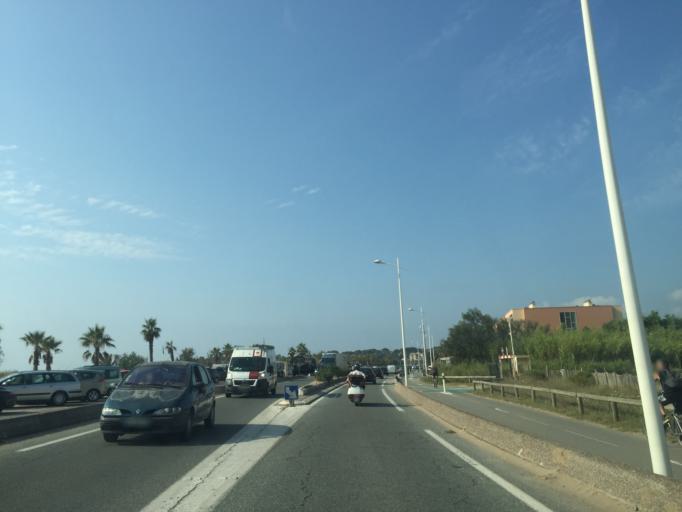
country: FR
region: Provence-Alpes-Cote d'Azur
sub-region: Departement du Var
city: Frejus
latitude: 43.3998
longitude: 6.7299
